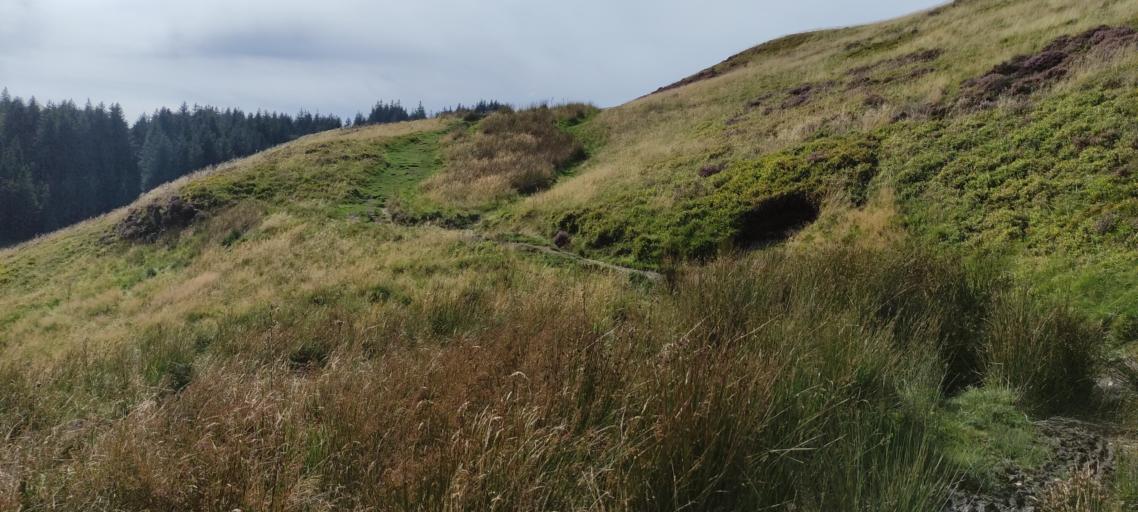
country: GB
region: England
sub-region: Cumbria
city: Keswick
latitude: 54.6303
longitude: -3.2233
